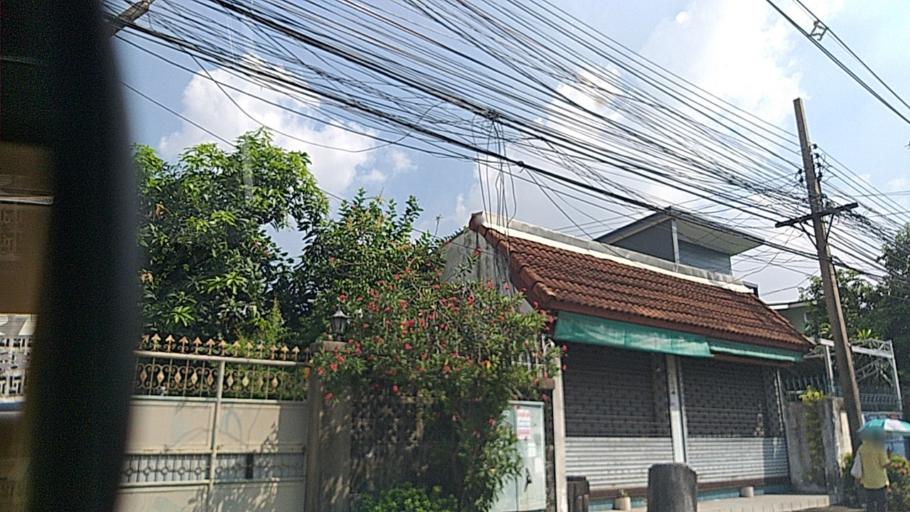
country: TH
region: Bangkok
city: Lat Phrao
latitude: 13.8203
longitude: 100.5946
